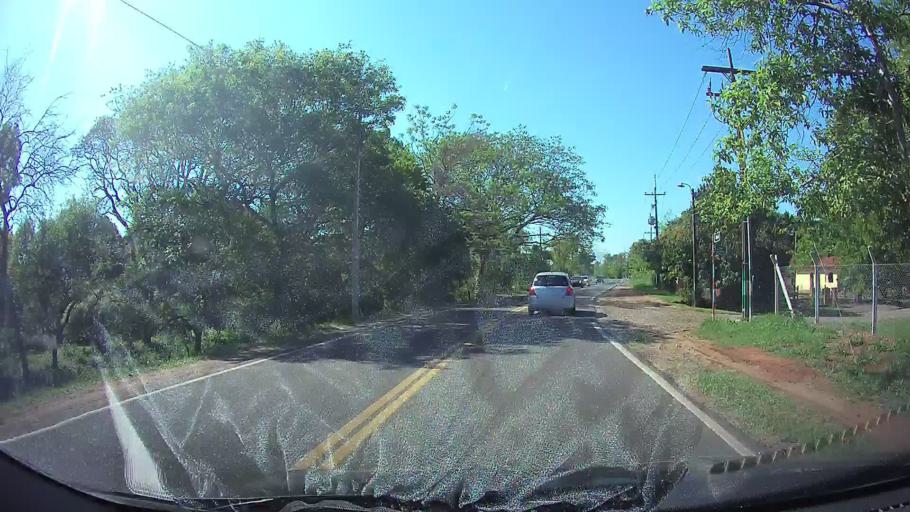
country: PY
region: Central
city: Ypacarai
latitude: -25.3959
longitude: -57.2937
